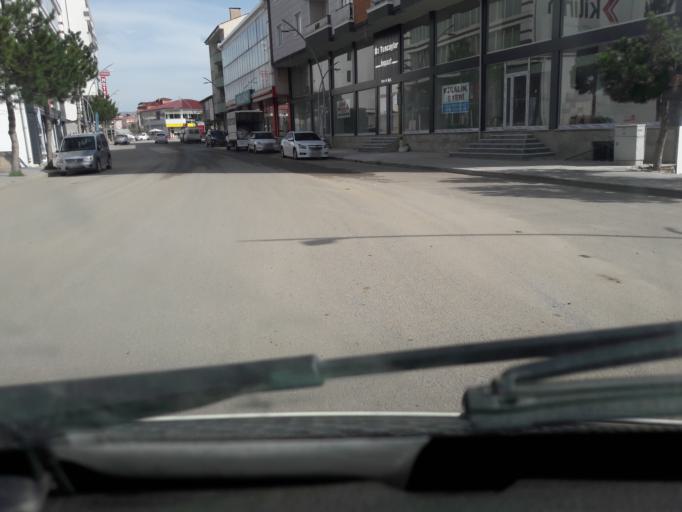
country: TR
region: Gumushane
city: Kelkit
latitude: 40.1347
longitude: 39.4344
